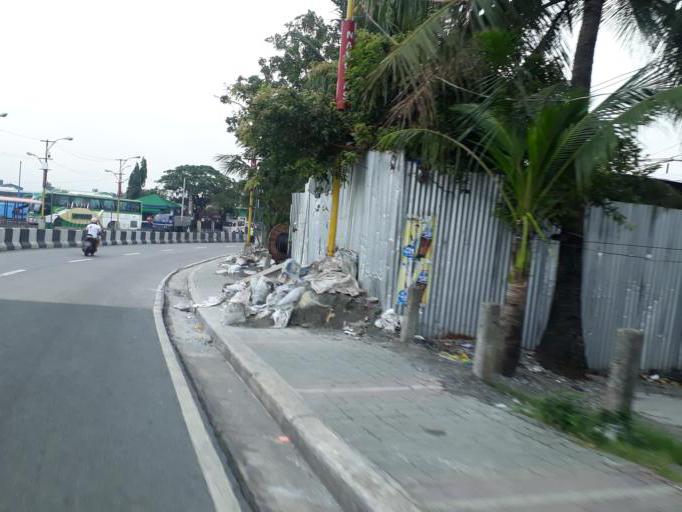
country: PH
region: Metro Manila
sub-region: Caloocan City
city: Niugan
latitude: 14.6509
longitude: 120.9479
